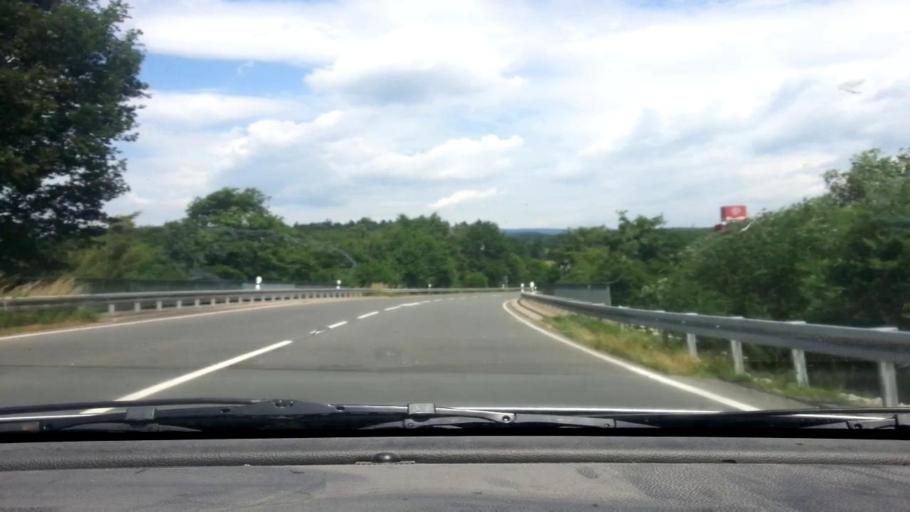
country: DE
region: Bavaria
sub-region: Upper Palatinate
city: Erbendorf
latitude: 49.8329
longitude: 12.0624
